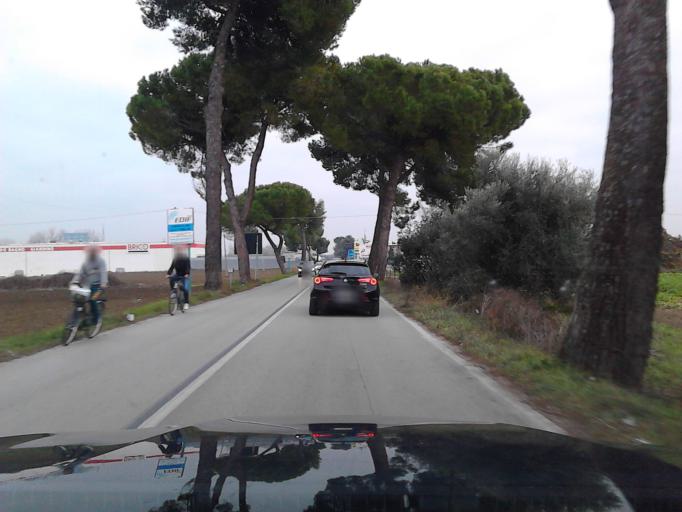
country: IT
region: Abruzzo
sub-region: Provincia di Teramo
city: Villa Rosa
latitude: 42.8333
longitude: 13.8959
